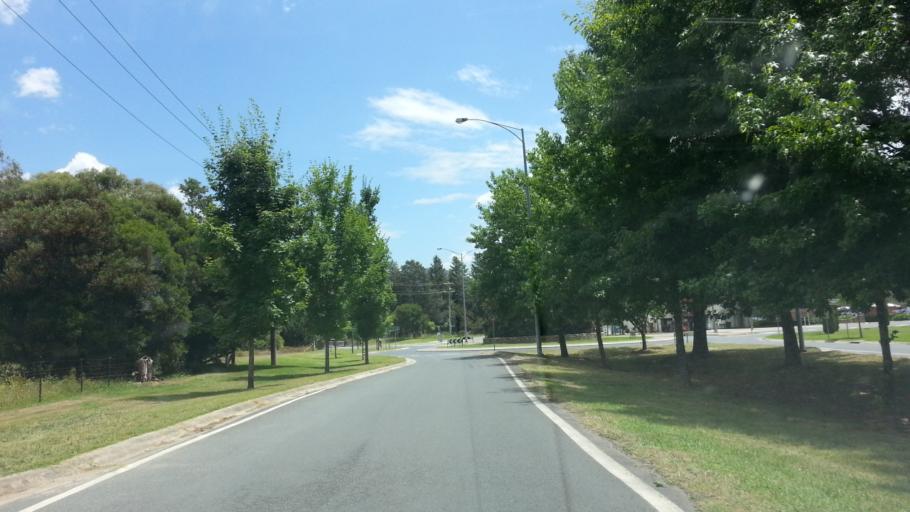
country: AU
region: Victoria
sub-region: Alpine
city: Mount Beauty
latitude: -36.7438
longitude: 147.1685
